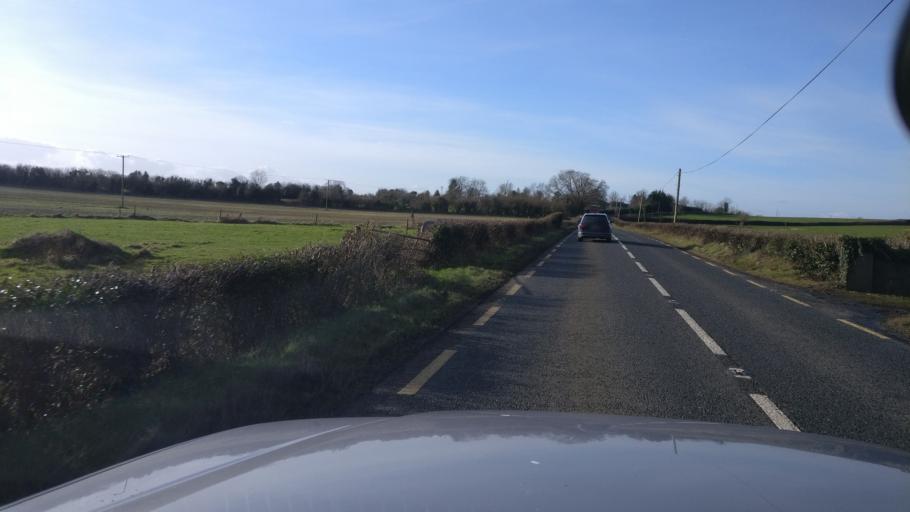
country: IE
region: Leinster
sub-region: Uibh Fhaili
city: Tullamore
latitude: 53.1985
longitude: -7.4248
